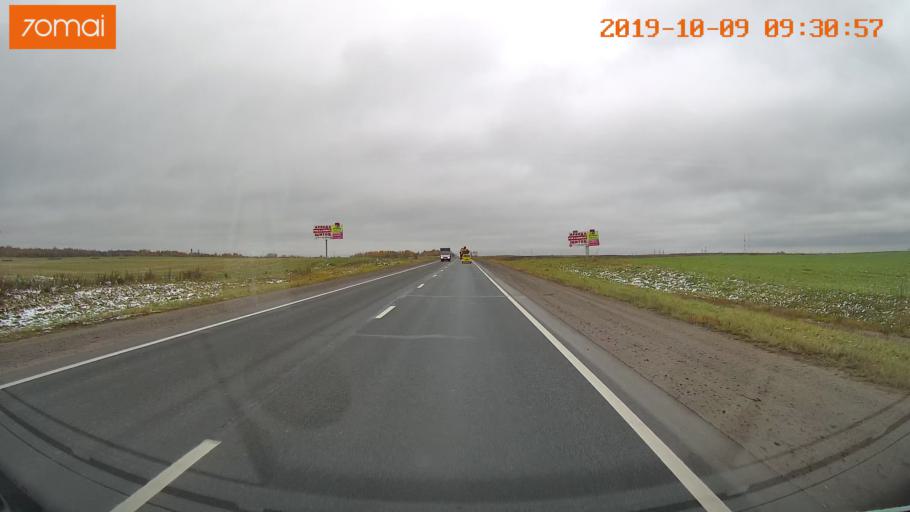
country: RU
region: Vologda
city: Vologda
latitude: 59.1449
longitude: 39.9437
